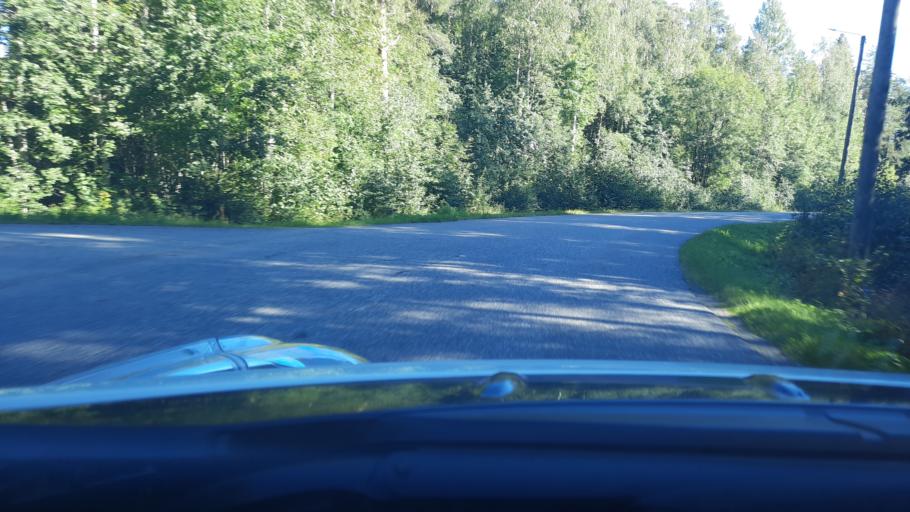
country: FI
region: North Karelia
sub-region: Joensuu
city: Joensuu
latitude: 62.6352
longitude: 29.6991
